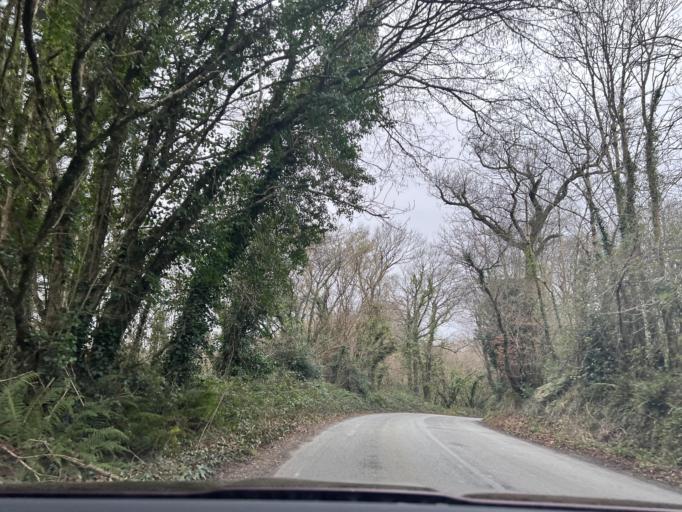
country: IE
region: Leinster
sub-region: Loch Garman
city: Castlebridge
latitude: 52.3800
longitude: -6.5360
